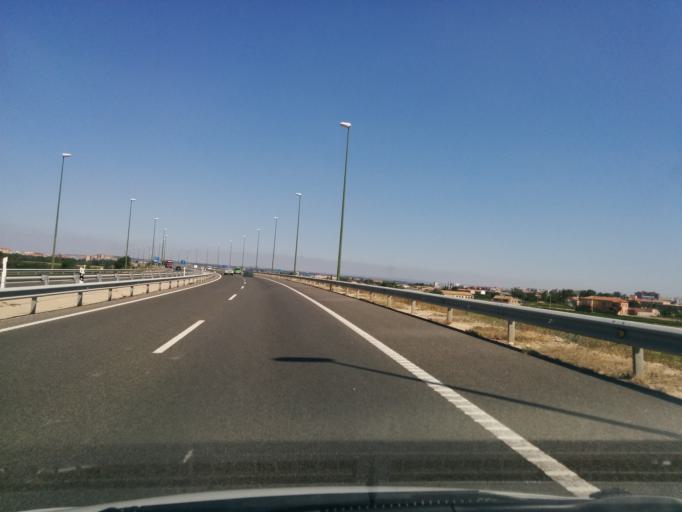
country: ES
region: Aragon
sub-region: Provincia de Zaragoza
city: Zaragoza
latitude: 41.6462
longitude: -0.8328
